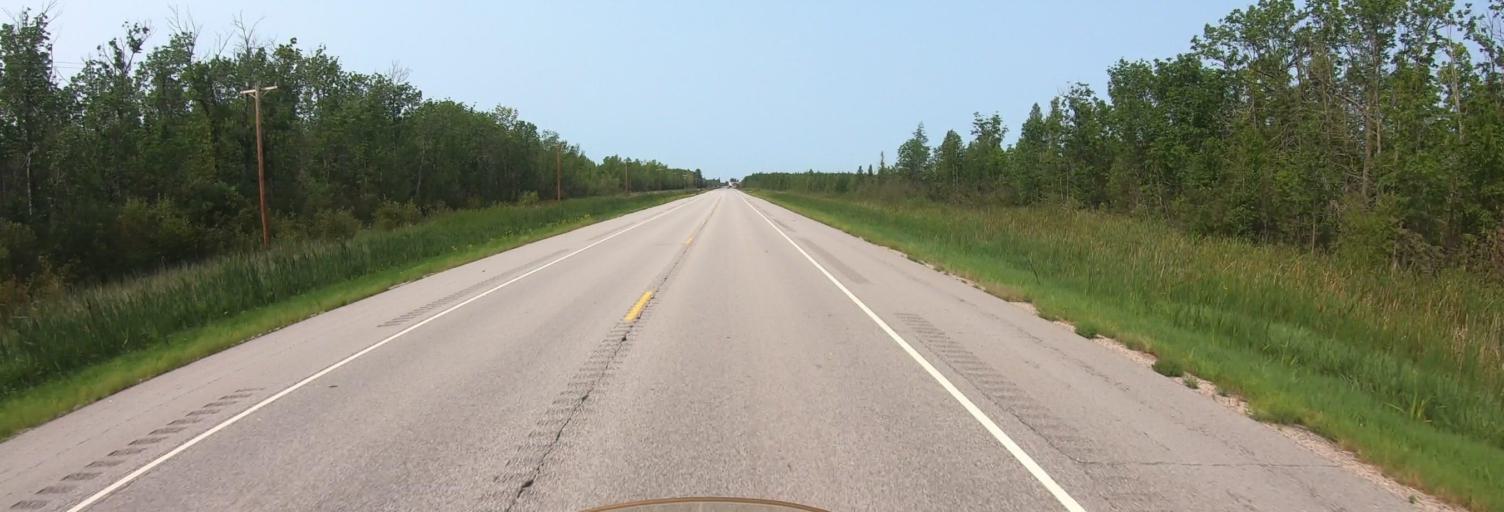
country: CA
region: Ontario
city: Fort Frances
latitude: 48.4104
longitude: -93.1821
